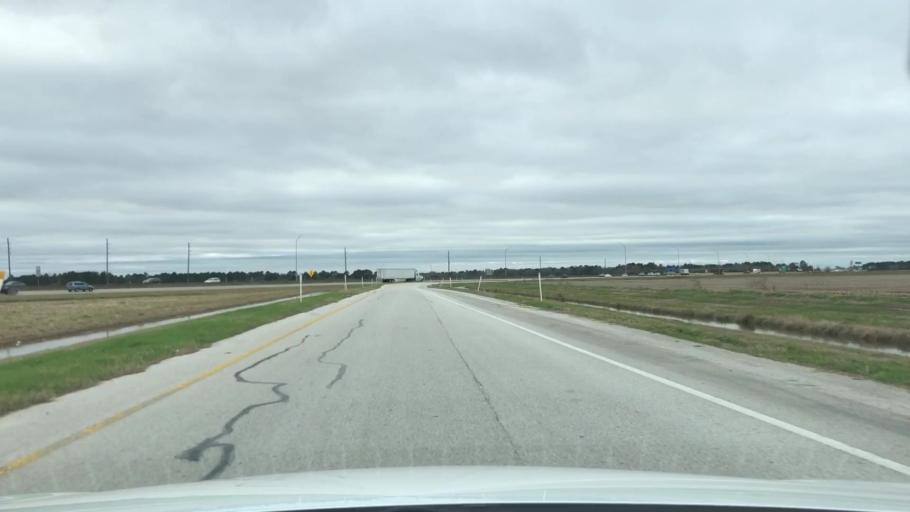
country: US
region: Texas
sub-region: Waller County
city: Brookshire
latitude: 29.7784
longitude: -95.9223
